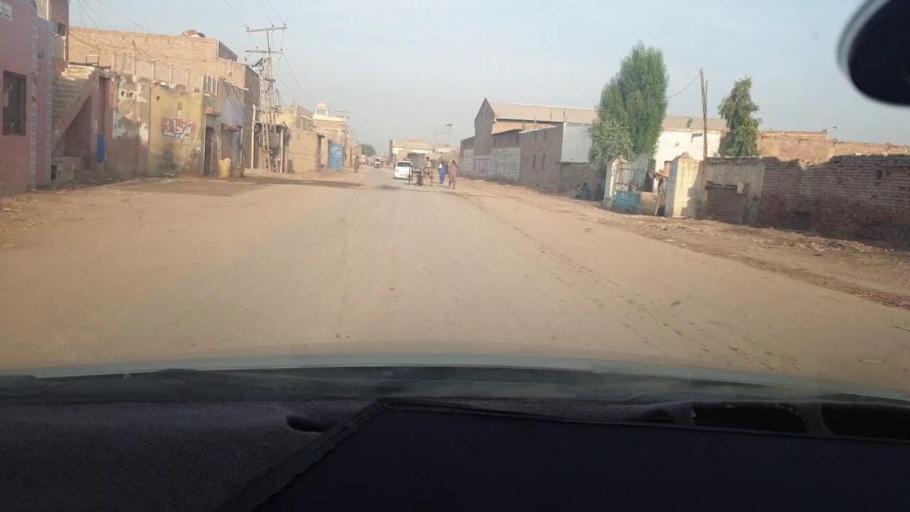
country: PK
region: Sindh
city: Jacobabad
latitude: 28.2836
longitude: 68.4273
